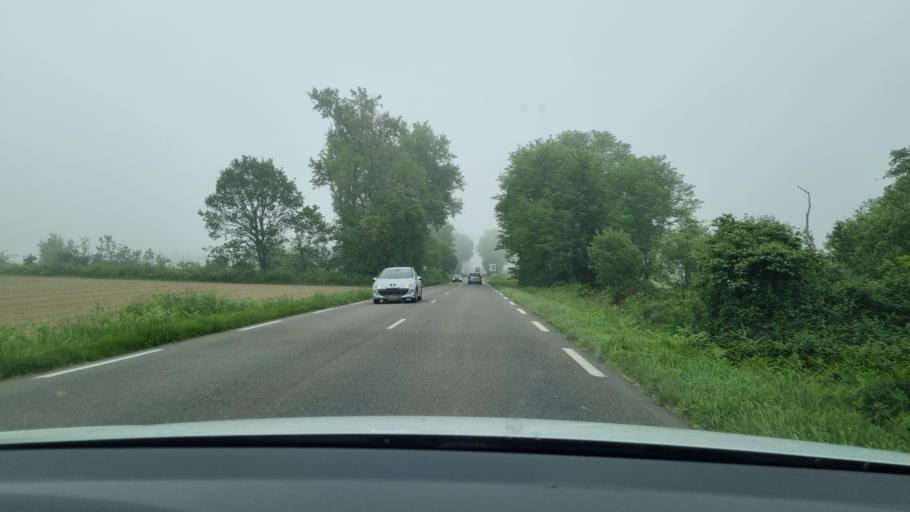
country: FR
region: Aquitaine
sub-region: Departement des Landes
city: Hagetmau
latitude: 43.6255
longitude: -0.6259
